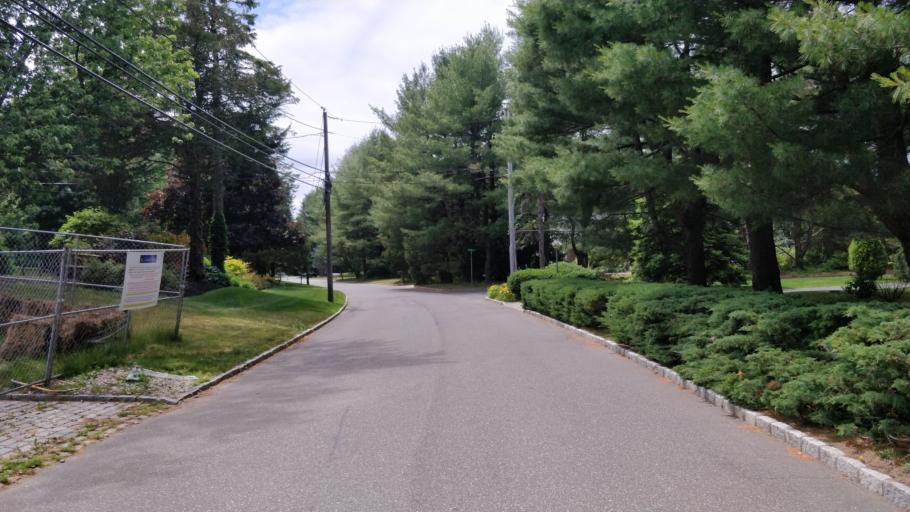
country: US
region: New York
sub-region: Nassau County
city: Laurel Hollow
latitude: 40.8415
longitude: -73.4743
